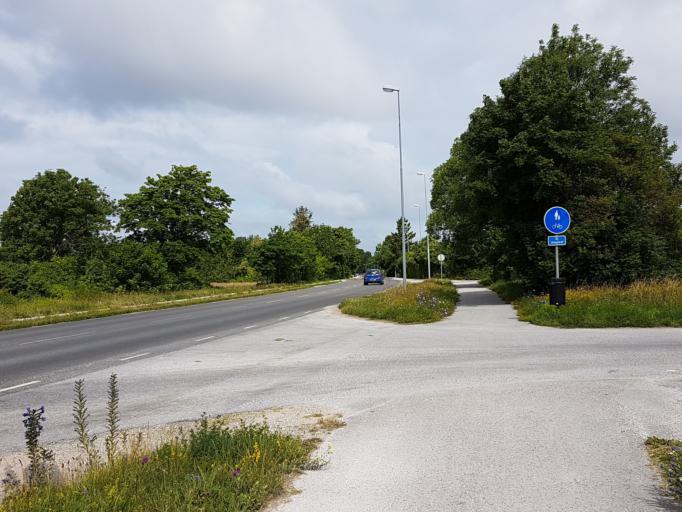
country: SE
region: Gotland
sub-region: Gotland
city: Visby
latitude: 57.6278
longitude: 18.3178
